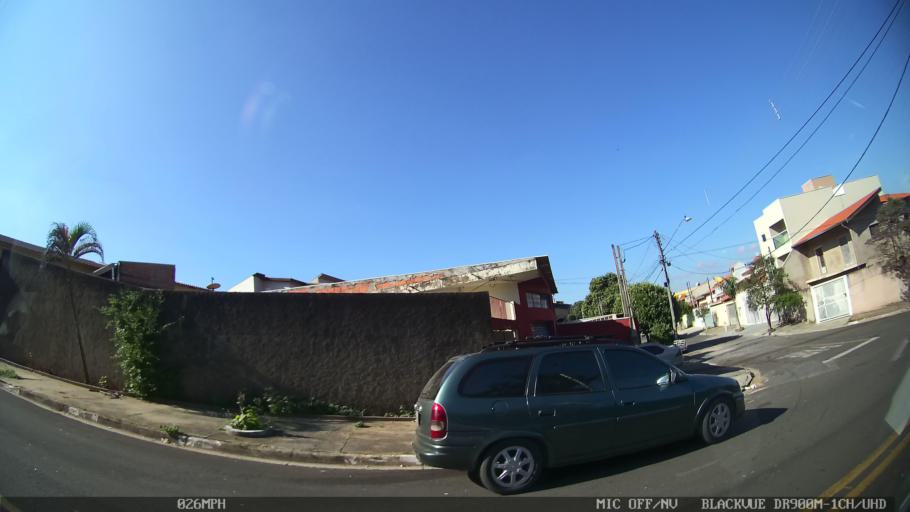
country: BR
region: Sao Paulo
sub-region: Campinas
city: Campinas
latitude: -22.9356
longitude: -47.1218
